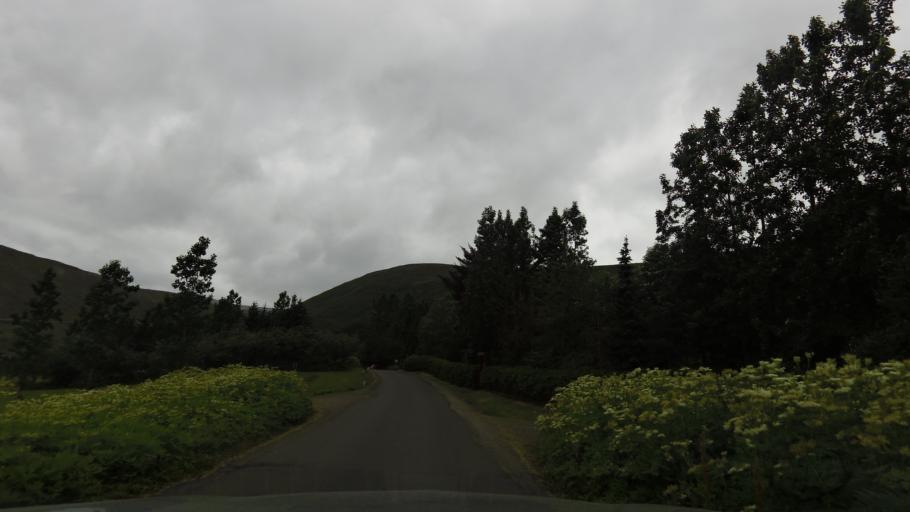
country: IS
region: Westfjords
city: Isafjoerdur
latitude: 66.0609
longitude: -23.1976
